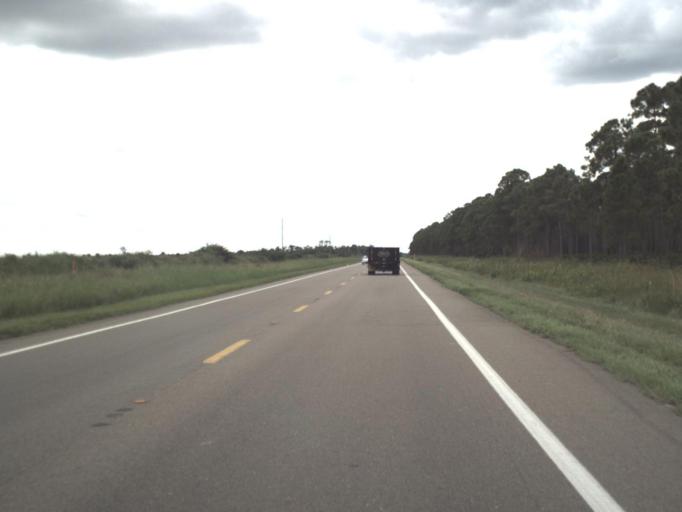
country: US
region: Florida
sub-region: Lee County
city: Olga
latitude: 26.8655
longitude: -81.7598
